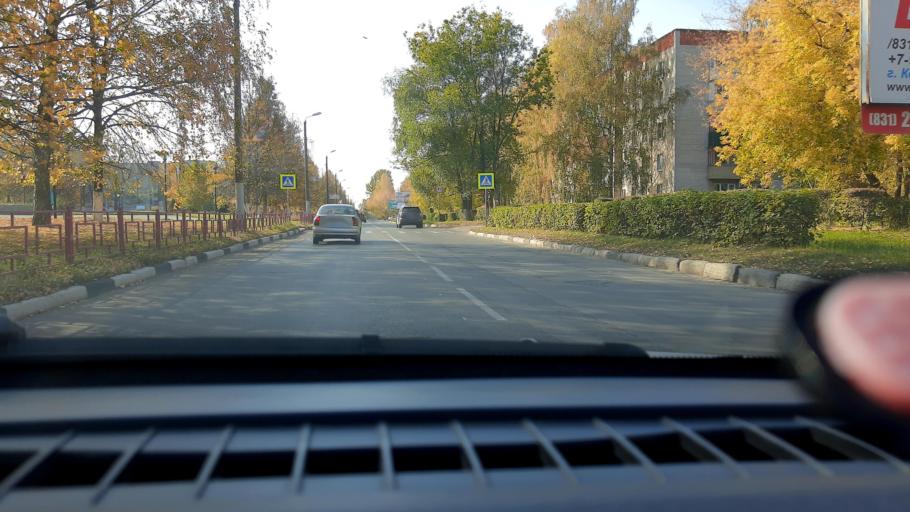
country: RU
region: Nizjnij Novgorod
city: Kstovo
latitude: 56.1434
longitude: 44.1910
